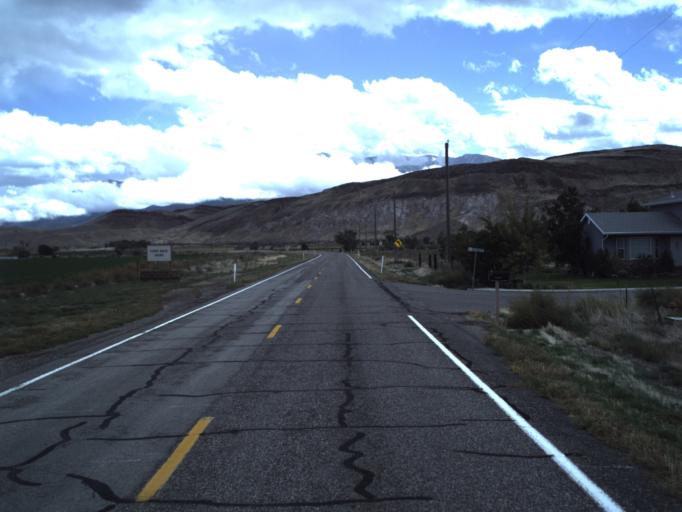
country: US
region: Utah
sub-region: Sevier County
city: Monroe
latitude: 38.6242
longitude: -112.2119
